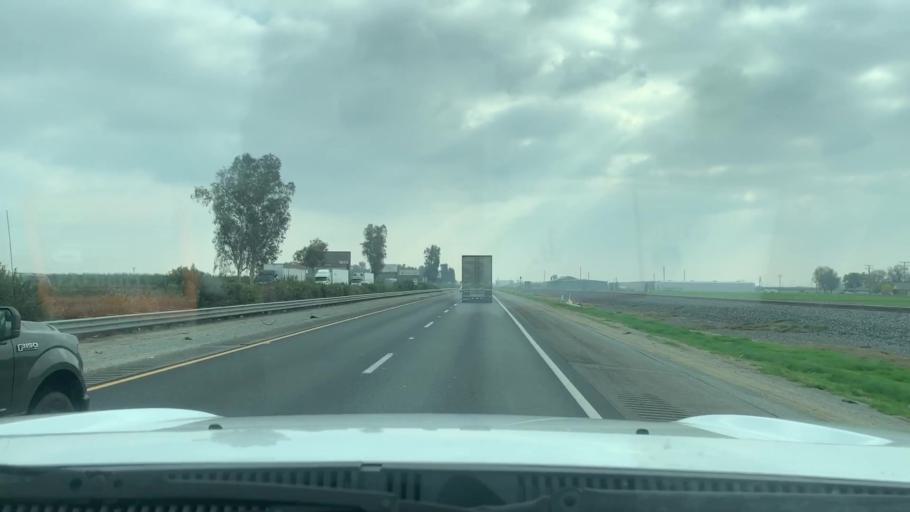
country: US
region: California
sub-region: Tulare County
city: Pixley
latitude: 35.9889
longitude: -119.2984
